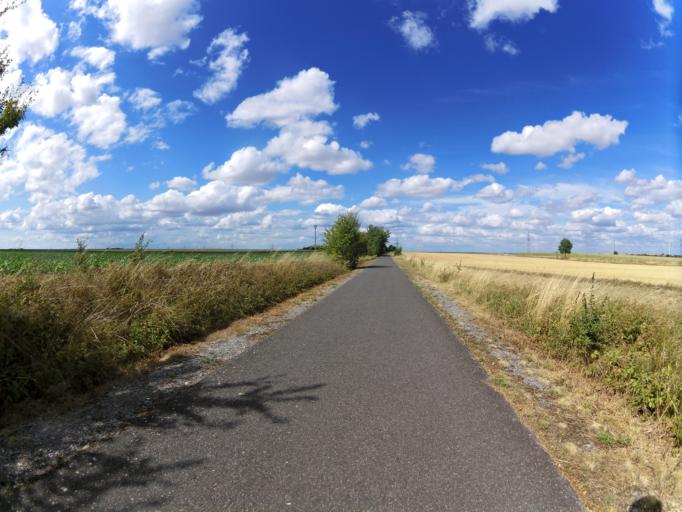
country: DE
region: Bavaria
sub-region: Regierungsbezirk Unterfranken
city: Sonderhofen
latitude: 49.5794
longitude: 10.0103
